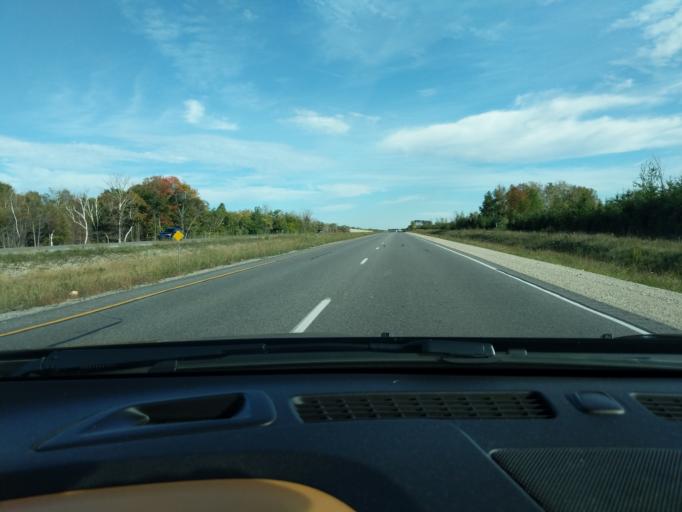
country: CA
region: Ontario
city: Collingwood
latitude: 44.4804
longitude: -80.1660
